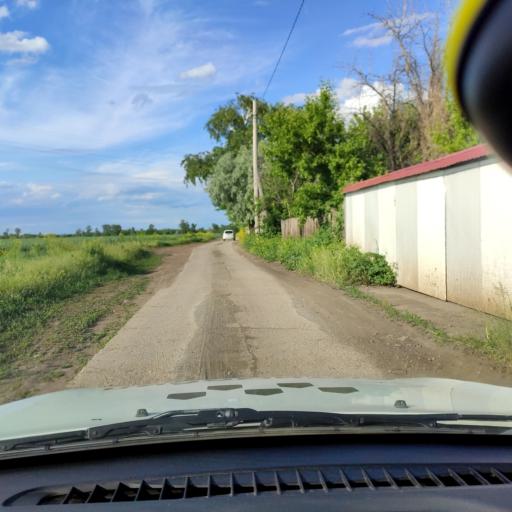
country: RU
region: Samara
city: Tol'yatti
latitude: 53.5913
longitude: 49.4514
